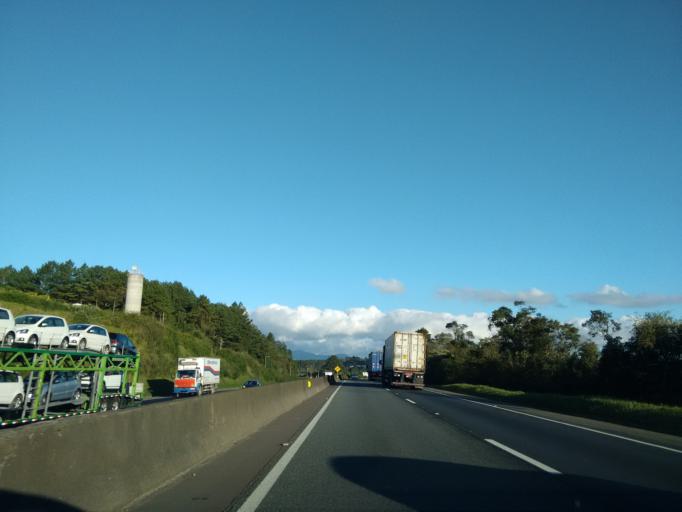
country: BR
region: Parana
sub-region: Sao Jose Dos Pinhais
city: Sao Jose dos Pinhais
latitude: -25.6333
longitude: -49.1623
